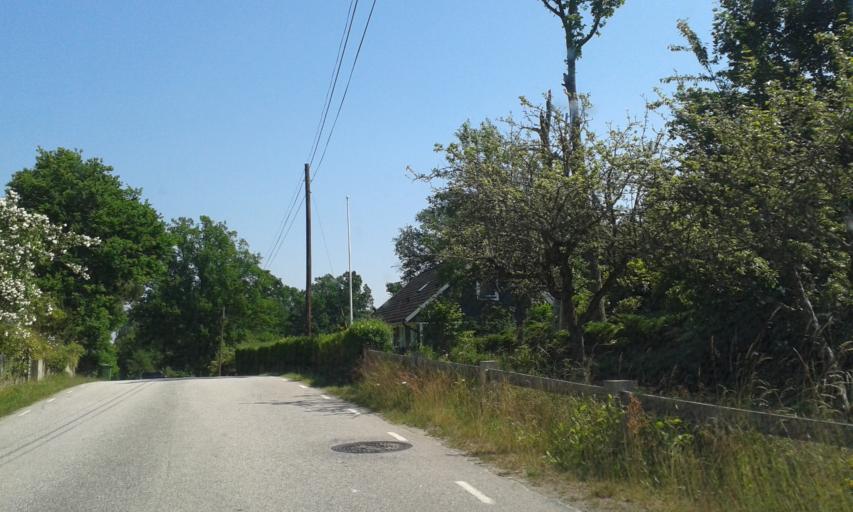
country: SE
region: Blekinge
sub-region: Karlskrona Kommun
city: Rodeby
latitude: 56.2306
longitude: 15.5801
